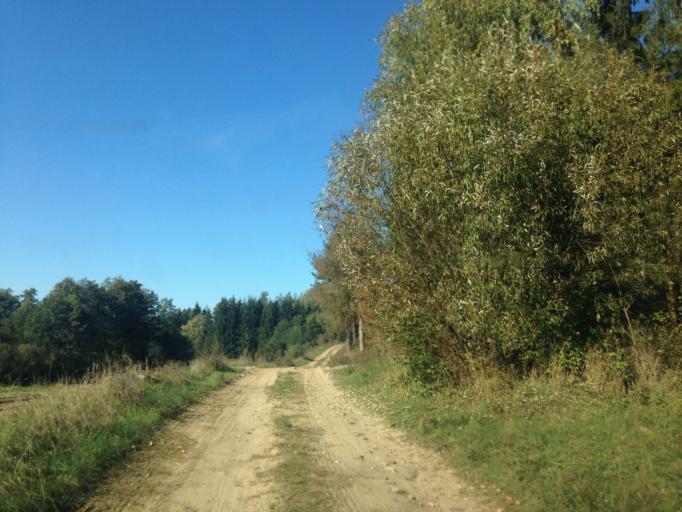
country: PL
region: Kujawsko-Pomorskie
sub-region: Powiat brodnicki
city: Bartniczka
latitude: 53.2746
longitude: 19.6313
